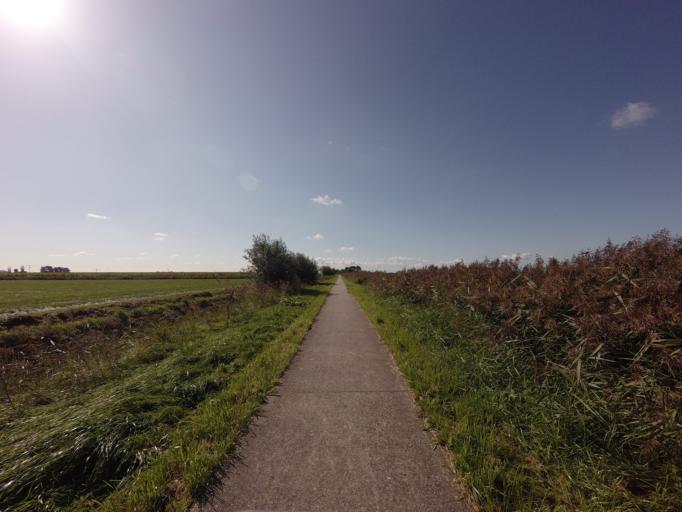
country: NL
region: Friesland
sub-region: Gemeente Boarnsterhim
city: Reduzum
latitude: 53.1337
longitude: 5.7577
